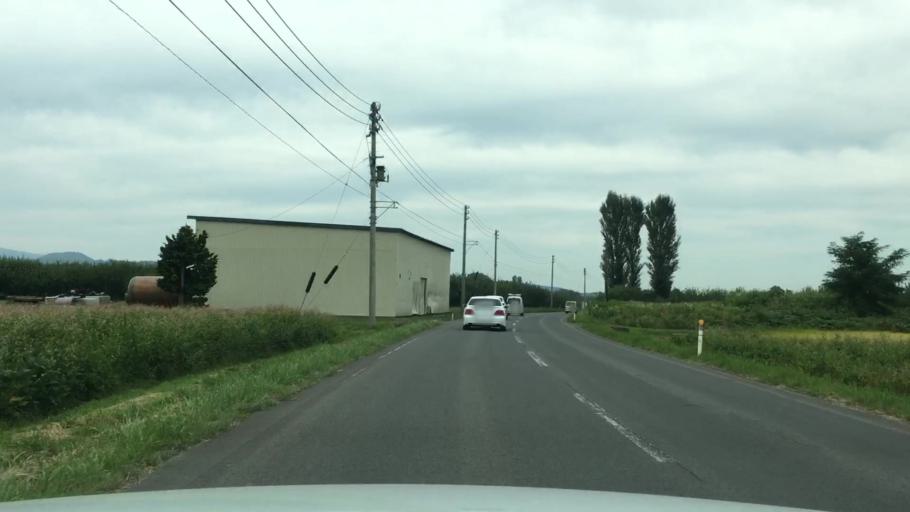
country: JP
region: Aomori
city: Hirosaki
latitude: 40.6460
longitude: 140.4243
